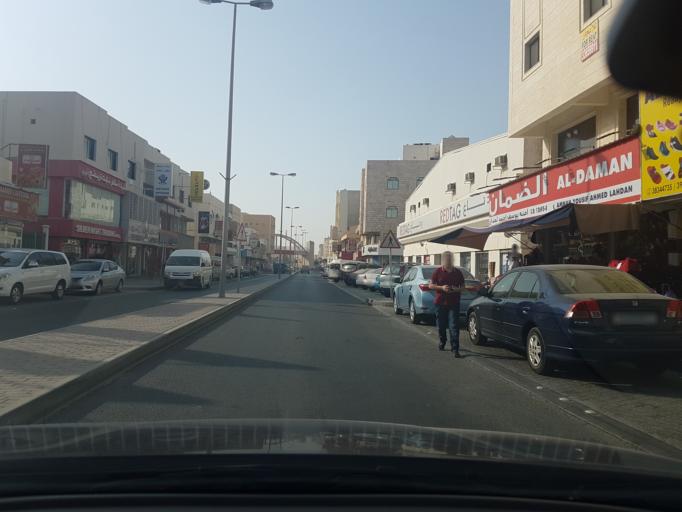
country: BH
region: Northern
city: Ar Rifa'
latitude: 26.1233
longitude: 50.5657
